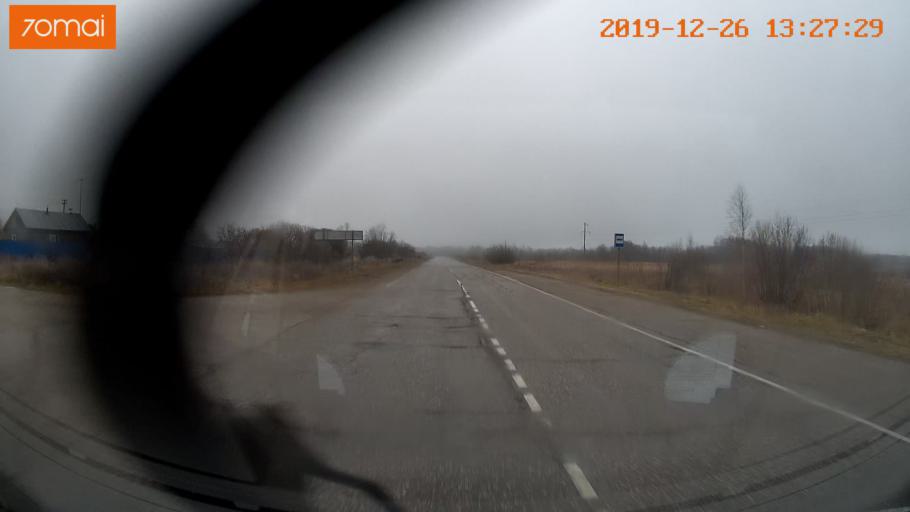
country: RU
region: Vologda
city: Cherepovets
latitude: 58.8534
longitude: 38.2403
